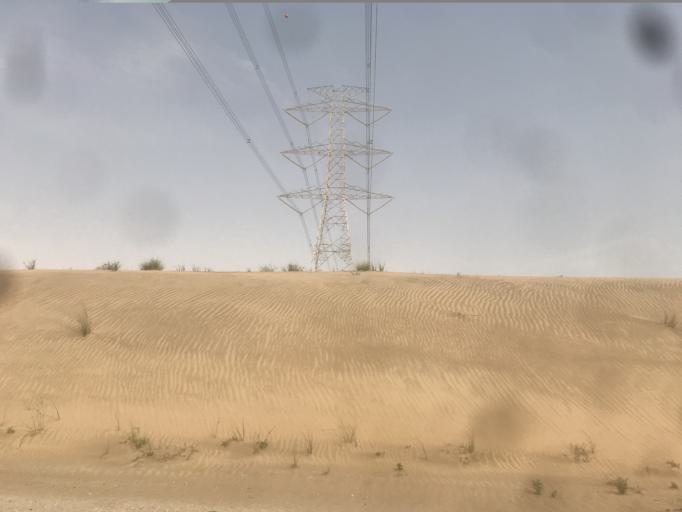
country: SA
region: Eastern Province
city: Abqaiq
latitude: 25.9074
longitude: 49.9042
